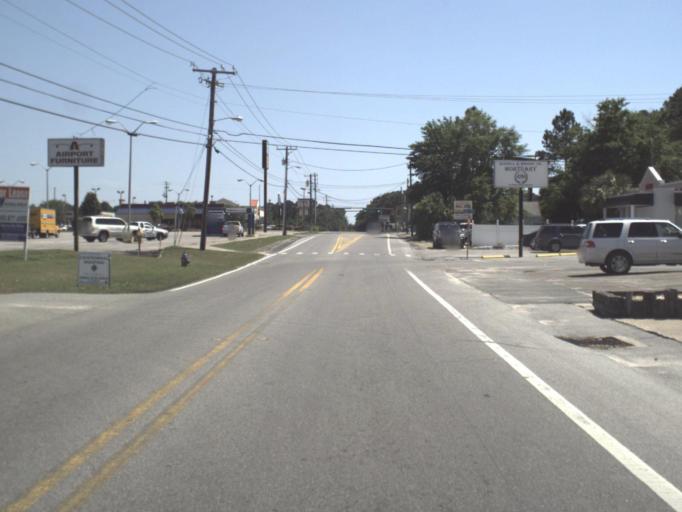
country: US
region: Florida
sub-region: Bay County
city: Pretty Bayou
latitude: 30.1776
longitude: -85.6837
